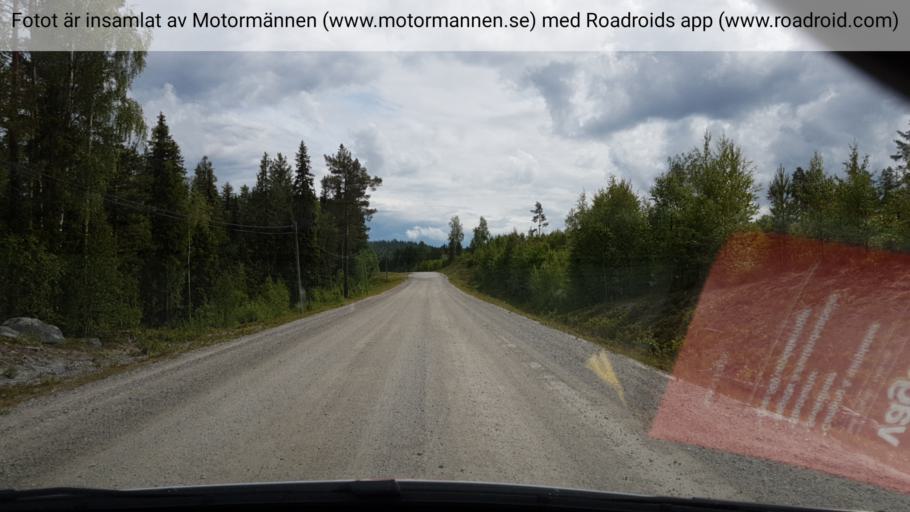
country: SE
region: Vaesternorrland
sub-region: Solleftea Kommun
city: Solleftea
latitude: 63.3889
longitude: 17.4959
